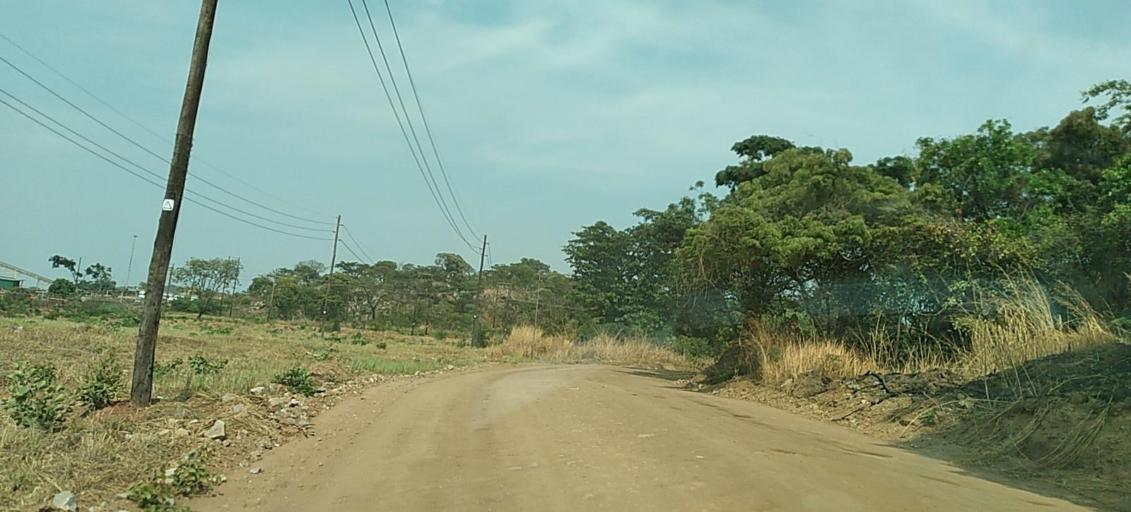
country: ZM
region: Copperbelt
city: Chililabombwe
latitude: -12.2949
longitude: 27.7703
